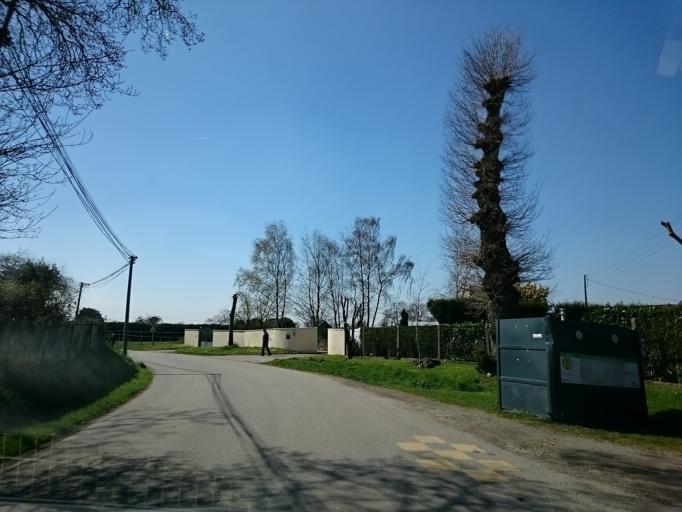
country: FR
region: Brittany
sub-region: Departement d'Ille-et-Vilaine
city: Crevin
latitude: 47.9643
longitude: -1.6817
